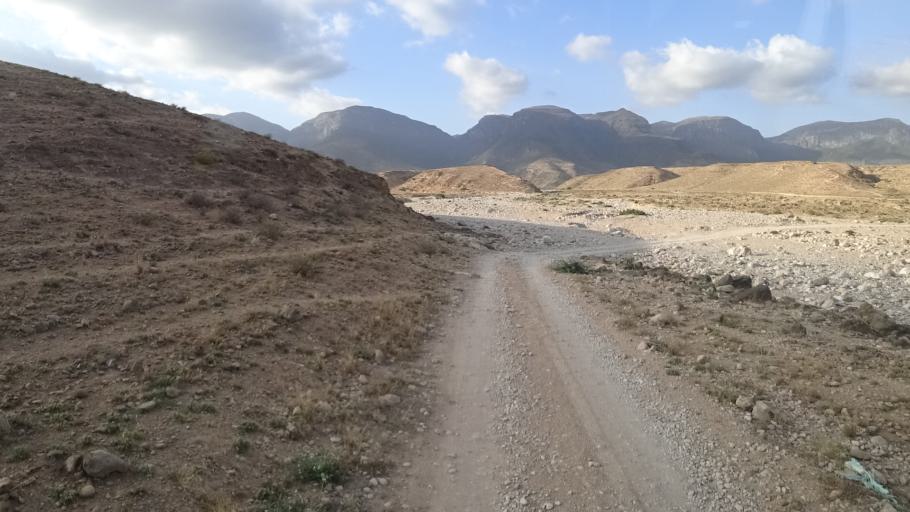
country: OM
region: Zufar
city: Salalah
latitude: 16.9767
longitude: 53.8524
